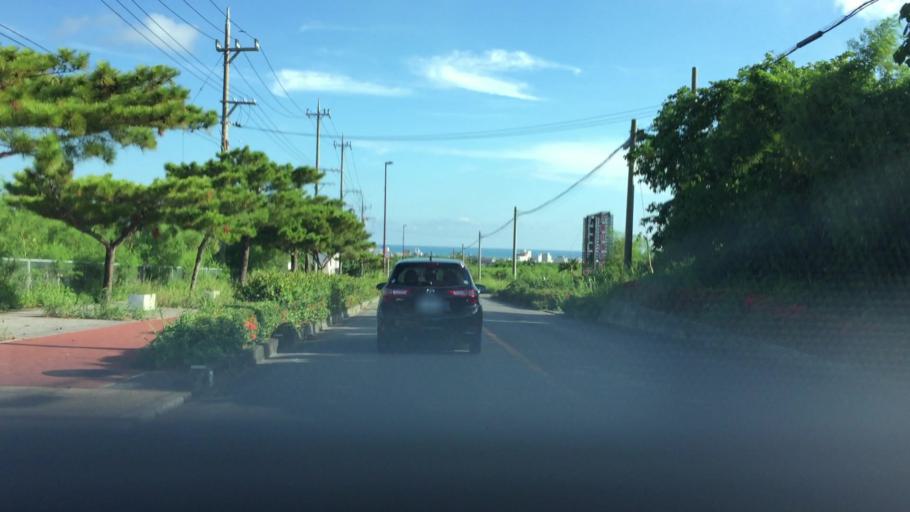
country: JP
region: Okinawa
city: Ishigaki
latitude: 24.3638
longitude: 124.1570
